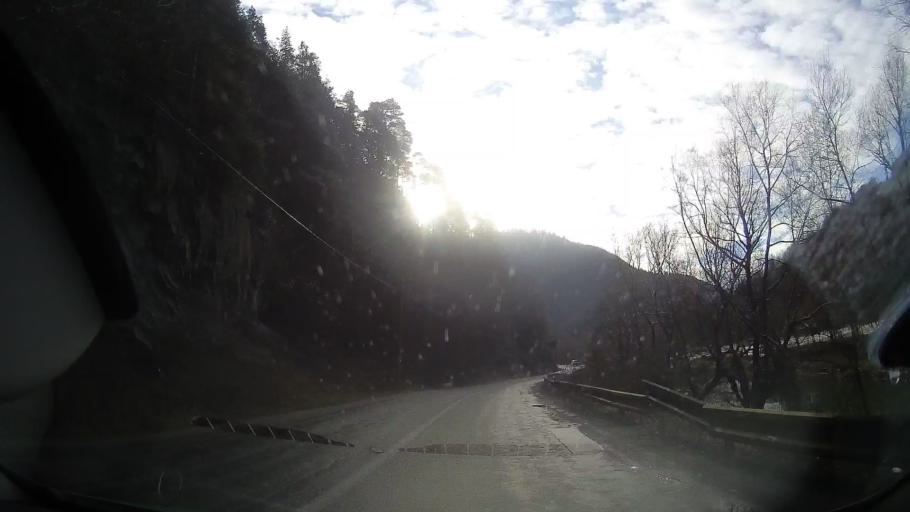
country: RO
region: Alba
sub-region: Comuna Bistra
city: Bistra
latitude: 46.3810
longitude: 23.1455
